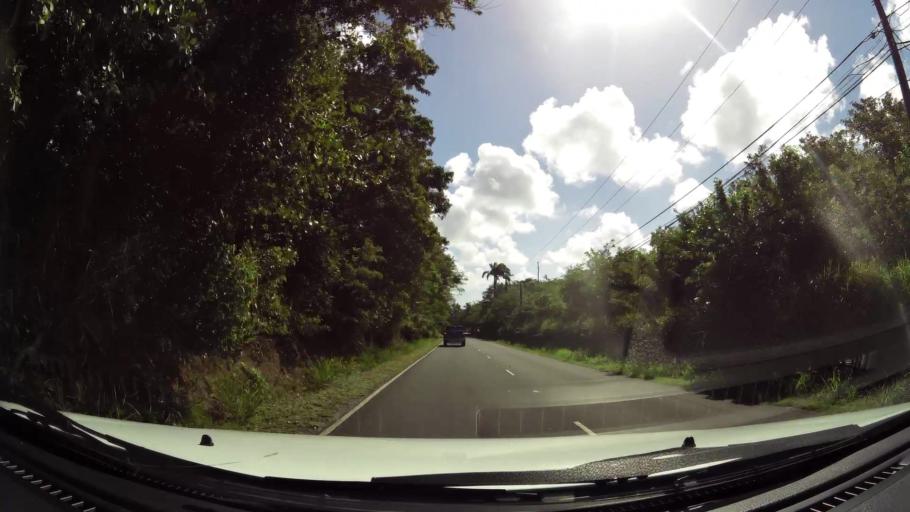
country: LC
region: Choiseul Quarter
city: Choiseul
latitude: 13.7599
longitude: -61.0266
